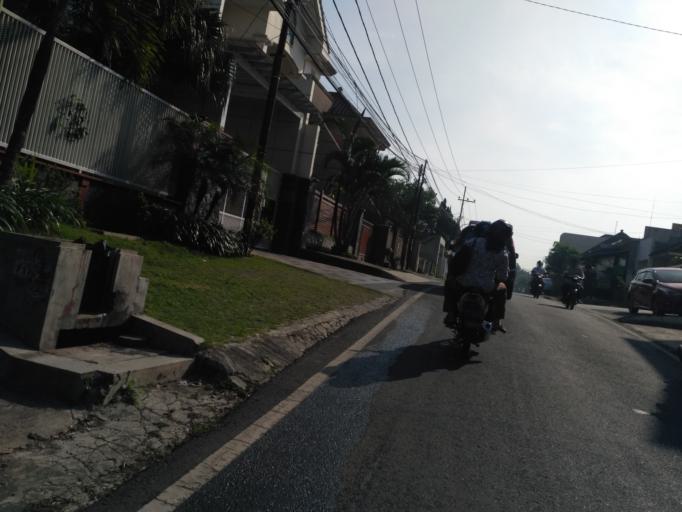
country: ID
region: East Java
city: Malang
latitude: -7.9511
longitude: 112.6226
